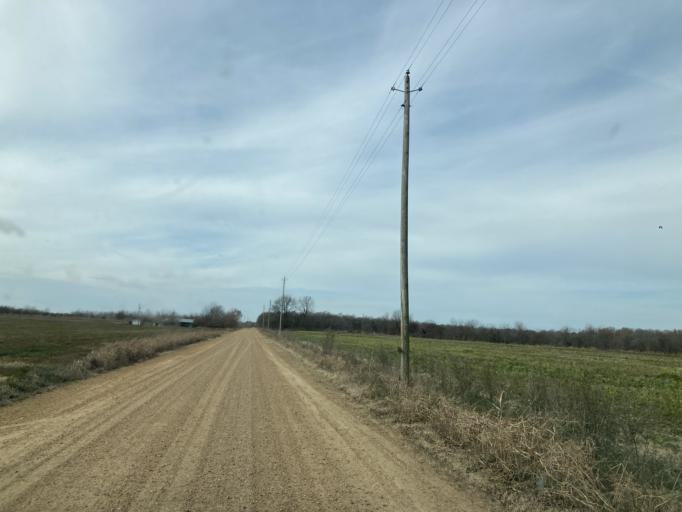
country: US
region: Mississippi
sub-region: Humphreys County
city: Belzoni
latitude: 33.1382
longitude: -90.6118
